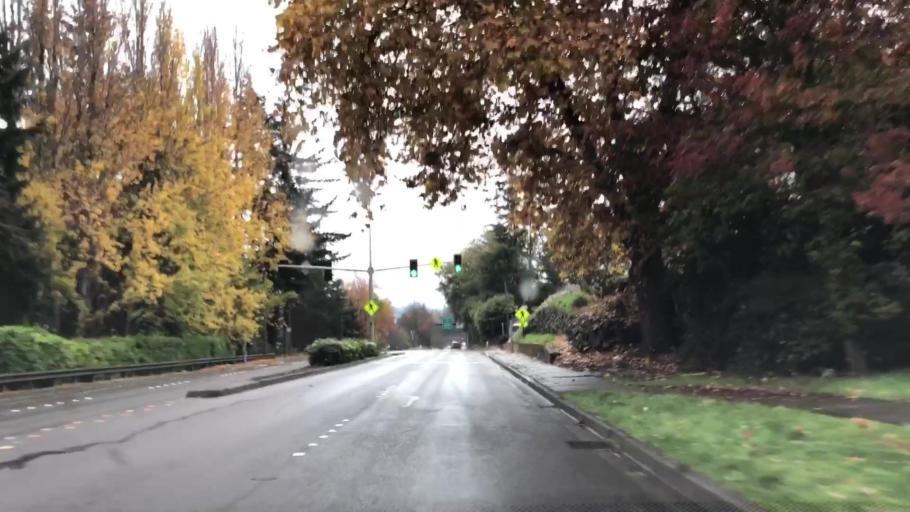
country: US
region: Washington
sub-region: King County
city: Mercer Island
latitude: 47.5811
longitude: -122.2306
